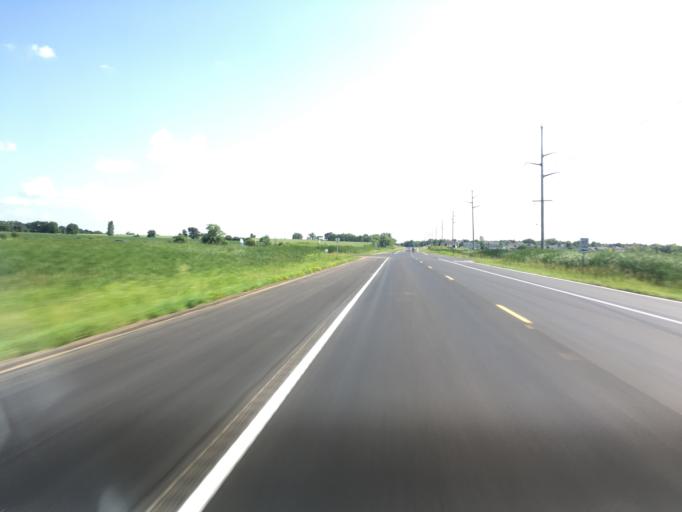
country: US
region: Minnesota
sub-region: Benton County
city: Sauk Rapids
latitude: 45.5890
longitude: -94.1329
